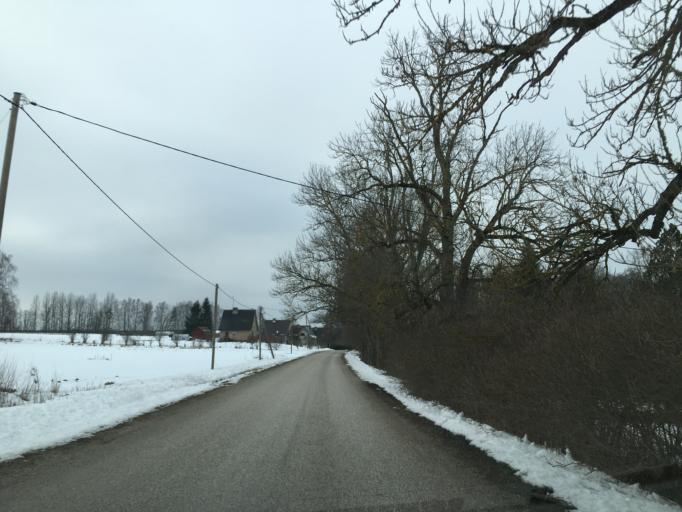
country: EE
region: Tartu
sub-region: Elva linn
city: Elva
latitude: 58.0989
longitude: 26.2069
